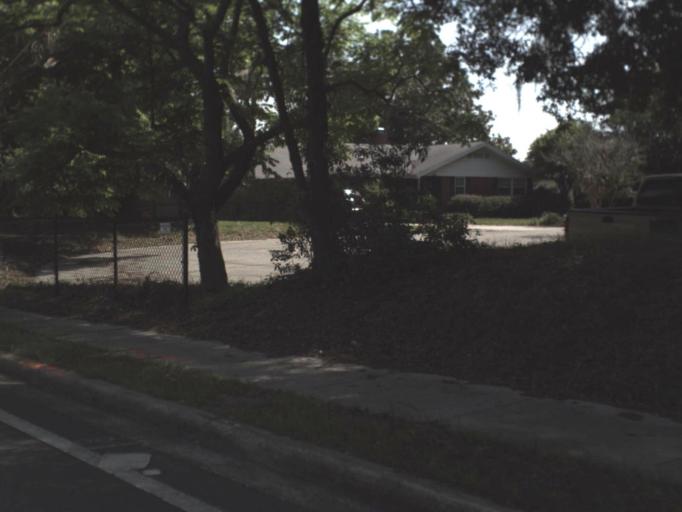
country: US
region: Florida
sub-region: Duval County
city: Jacksonville
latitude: 30.3205
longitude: -81.5984
